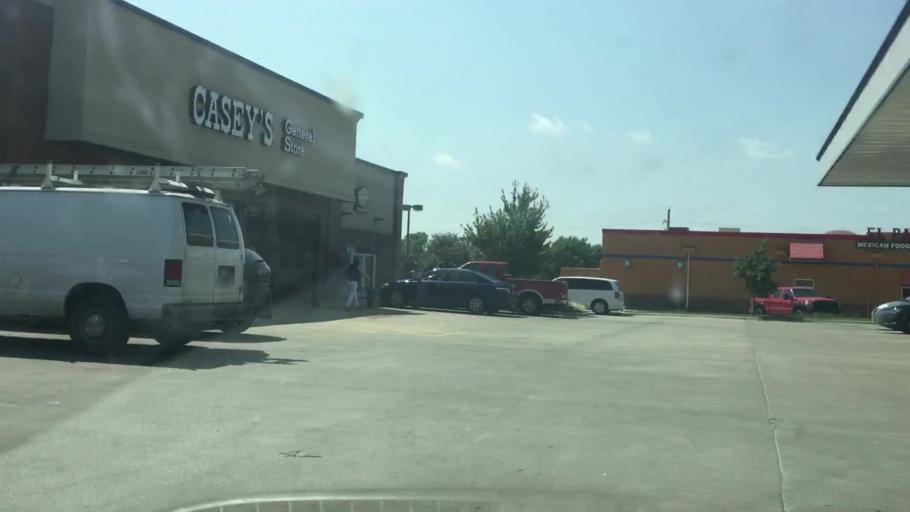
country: US
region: Kansas
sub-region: Johnson County
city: De Soto
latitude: 38.9636
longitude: -94.9837
